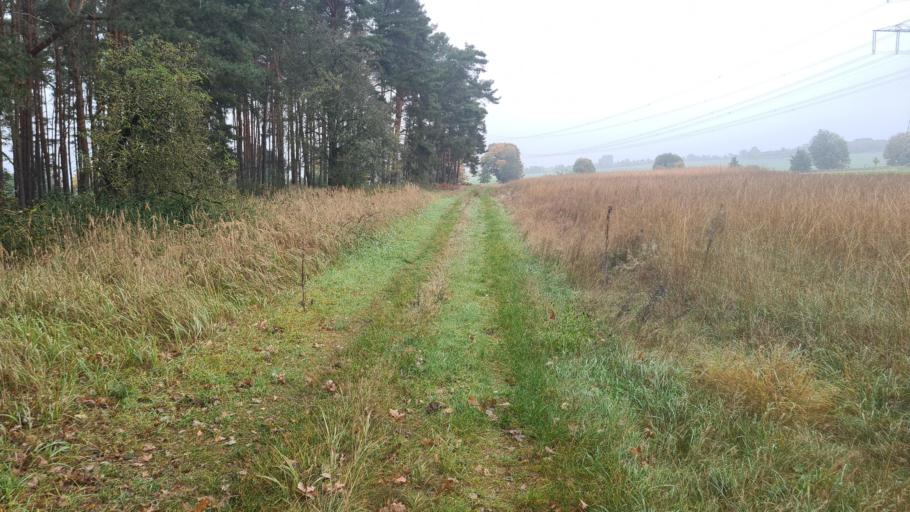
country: DE
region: Brandenburg
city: Furstenwalde
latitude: 52.4267
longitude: 14.0118
